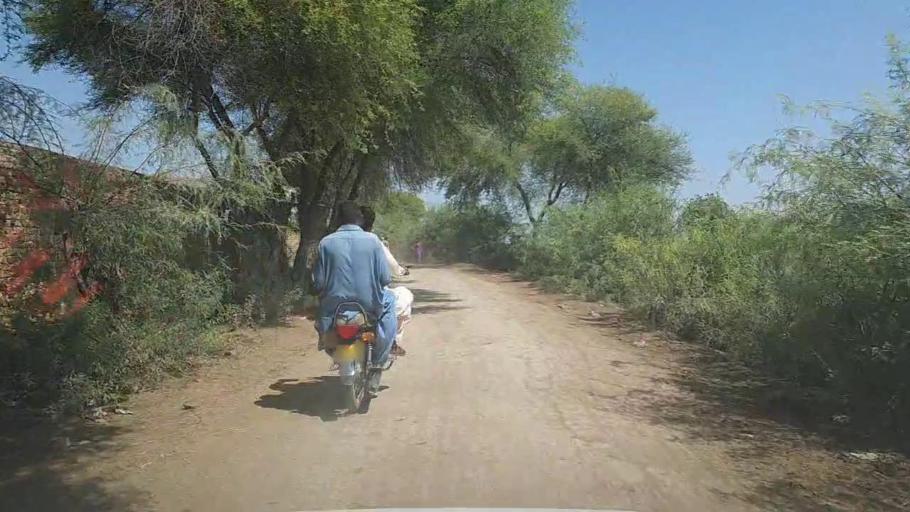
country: PK
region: Sindh
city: Kashmor
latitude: 28.2988
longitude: 69.4258
